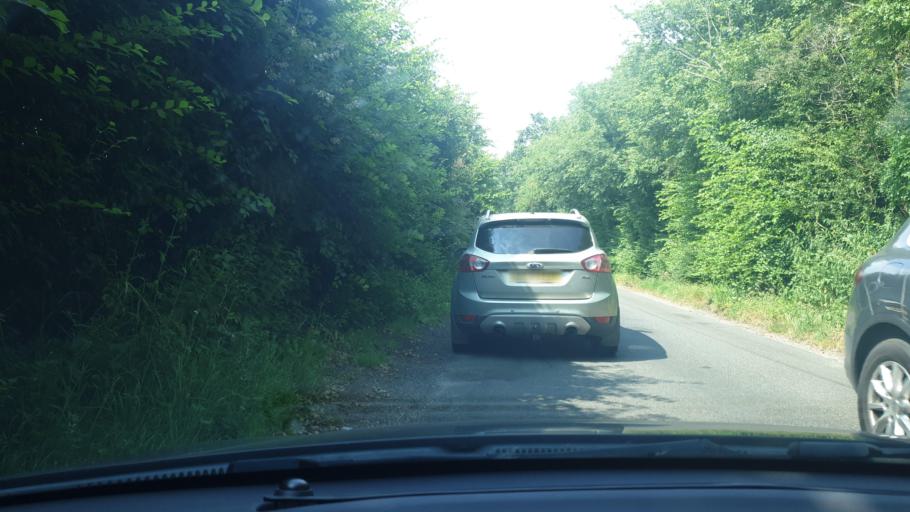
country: GB
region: England
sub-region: Essex
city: Manningtree
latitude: 51.9408
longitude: 1.0312
